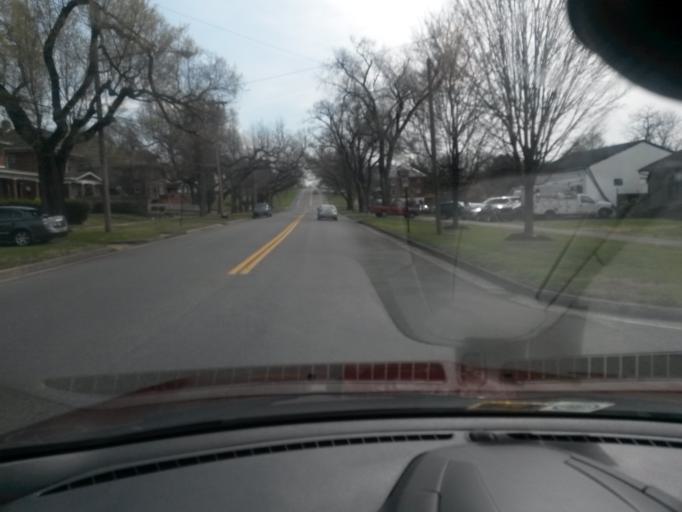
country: US
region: Virginia
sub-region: City of Roanoke
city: Roanoke
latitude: 37.2746
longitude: -79.9739
